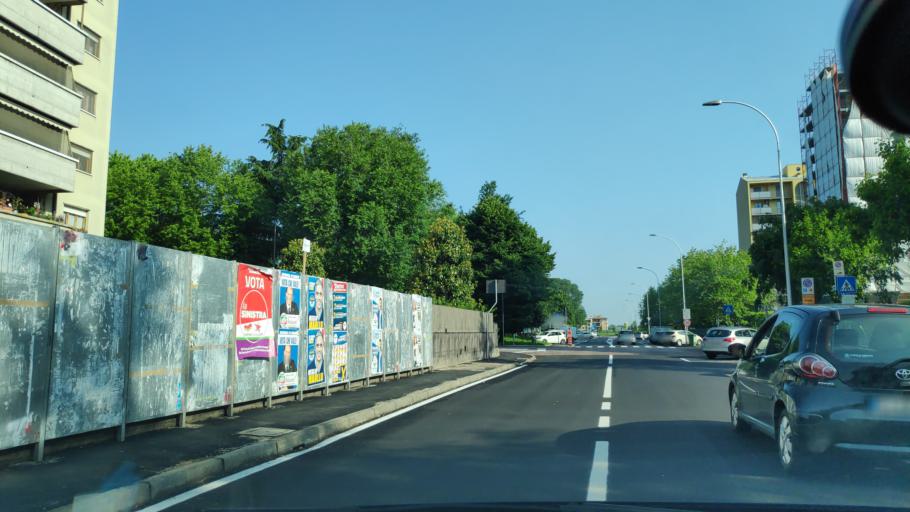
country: IT
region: Lombardy
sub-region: Citta metropolitana di Milano
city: Locate di Triulzi
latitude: 45.3579
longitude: 9.2303
